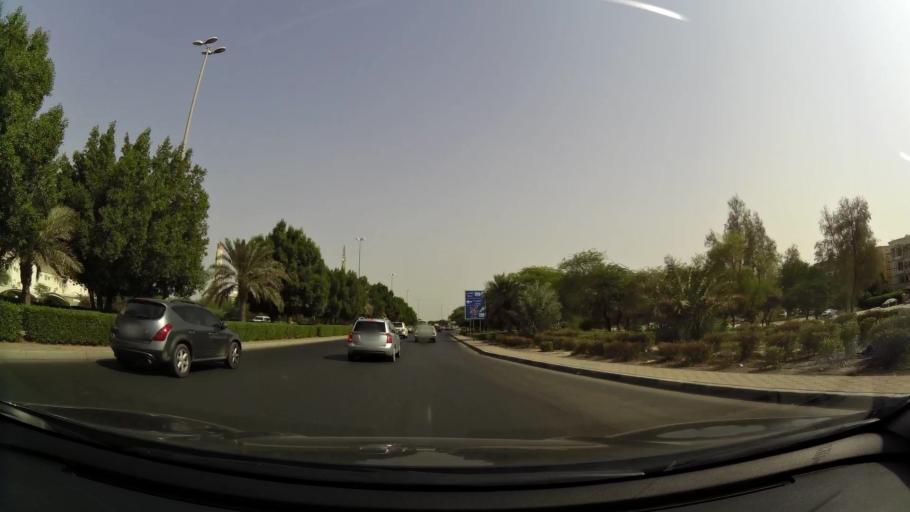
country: KW
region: Muhafazat al Jahra'
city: Al Jahra'
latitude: 29.3364
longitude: 47.6634
